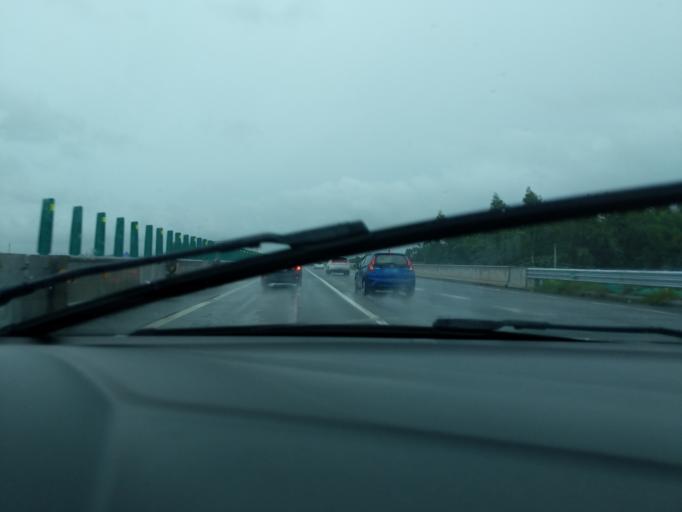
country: CN
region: Guangdong
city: Yueshan
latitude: 22.4576
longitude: 112.6840
